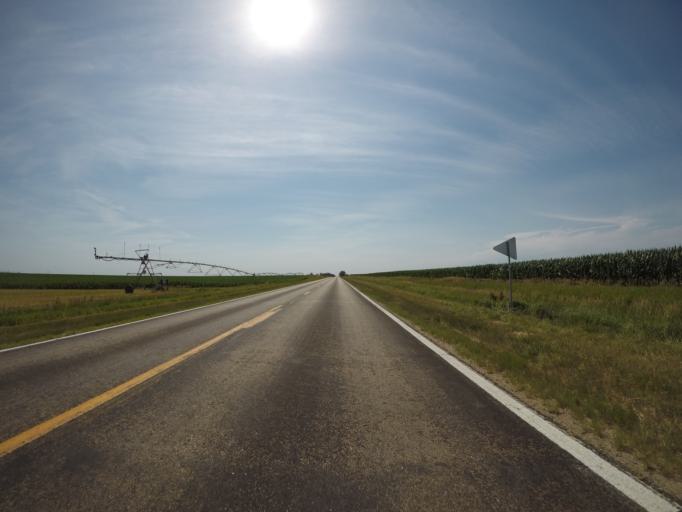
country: US
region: Nebraska
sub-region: Adams County
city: Hastings
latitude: 40.4374
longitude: -98.4658
